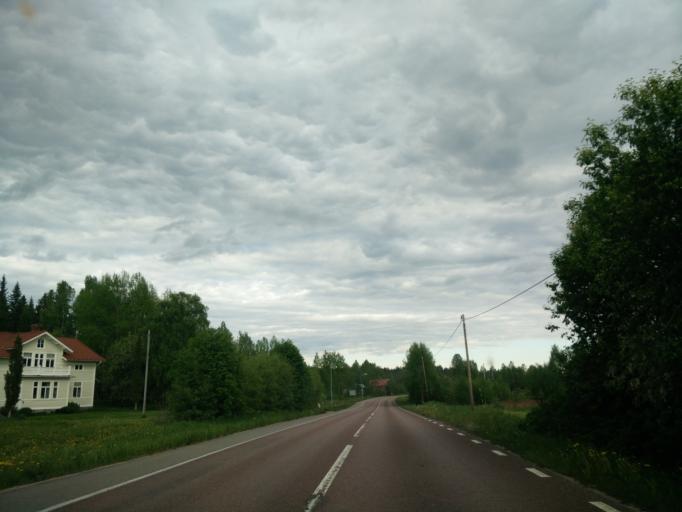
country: SE
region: Jaemtland
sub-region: Harjedalens Kommun
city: Sveg
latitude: 62.2947
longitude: 14.7865
